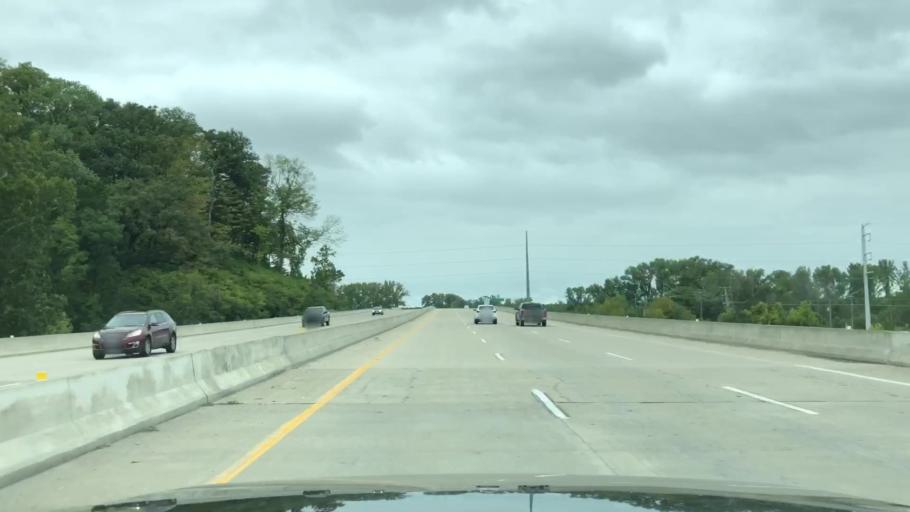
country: US
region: Missouri
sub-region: Saint Louis County
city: Maryland Heights
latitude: 38.6909
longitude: -90.4977
